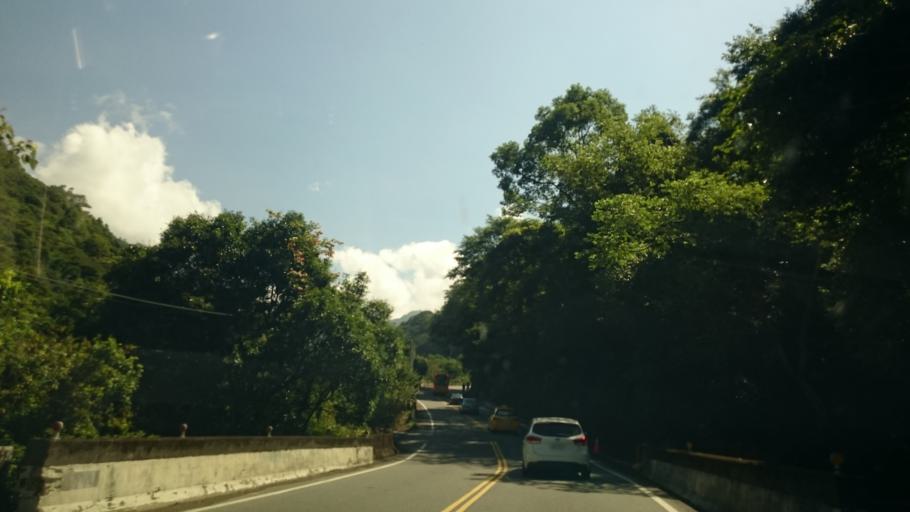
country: TW
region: Taiwan
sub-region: Nantou
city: Puli
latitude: 24.0093
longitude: 121.1150
